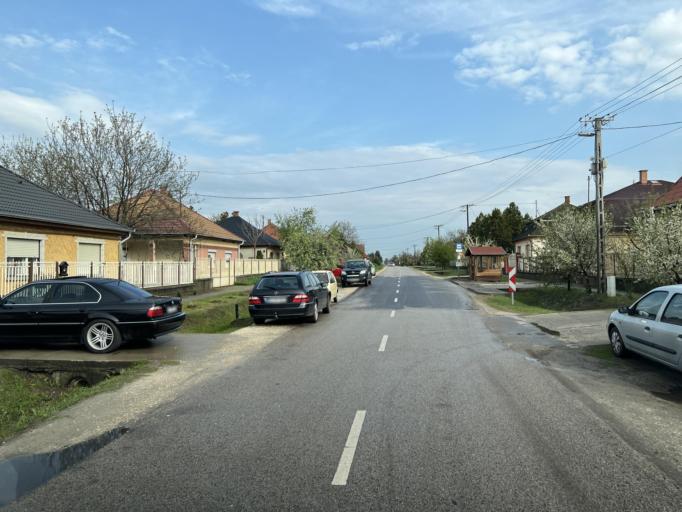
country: HU
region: Pest
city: Nyaregyhaza
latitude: 47.2222
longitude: 19.4586
